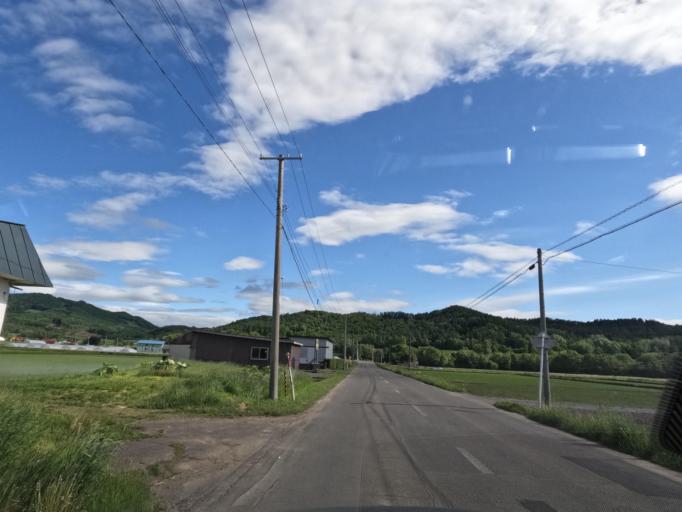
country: JP
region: Hokkaido
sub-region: Asahikawa-shi
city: Asahikawa
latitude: 43.7536
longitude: 142.5252
